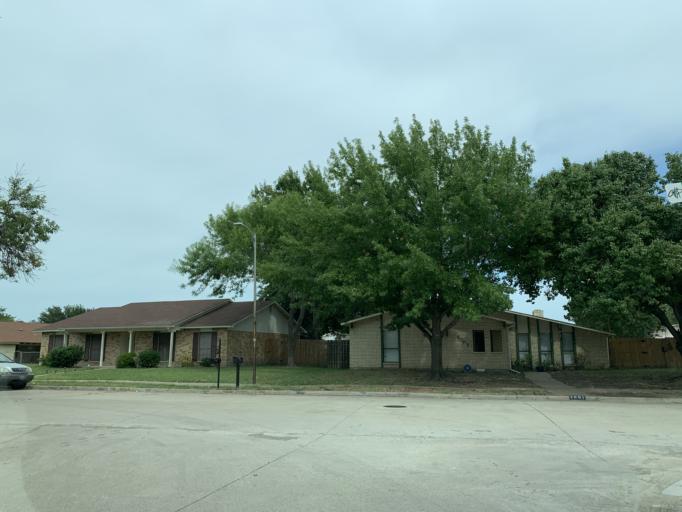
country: US
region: Texas
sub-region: Dallas County
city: Cedar Hill
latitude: 32.6515
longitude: -97.0320
